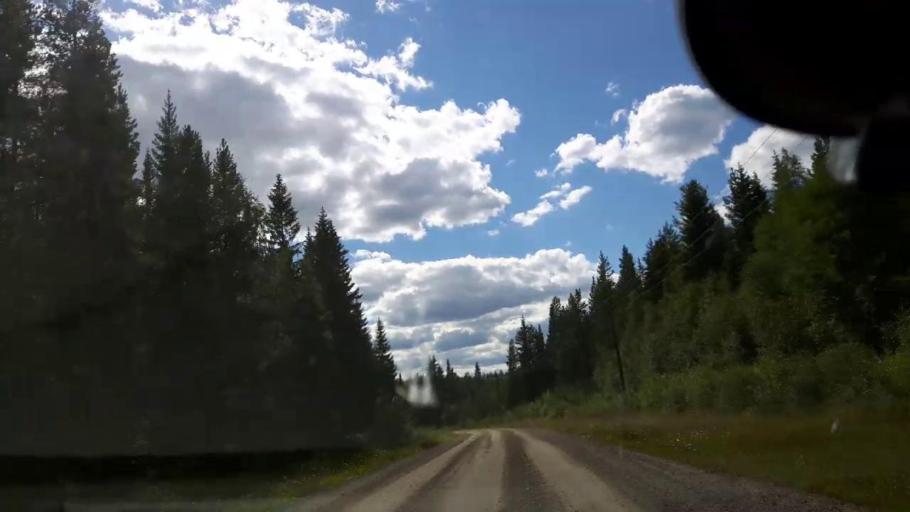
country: SE
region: Vaesternorrland
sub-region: Ange Kommun
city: Ange
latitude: 62.7679
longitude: 15.7379
